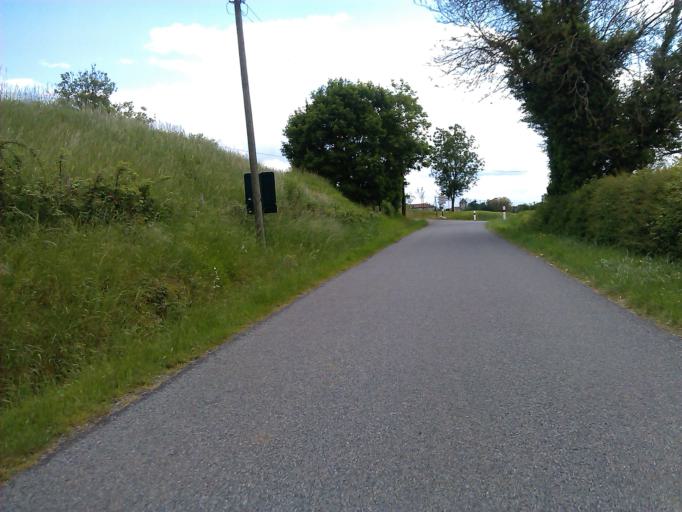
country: FR
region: Poitou-Charentes
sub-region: Departement de la Charente
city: Mansle
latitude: 45.9421
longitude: 0.2465
